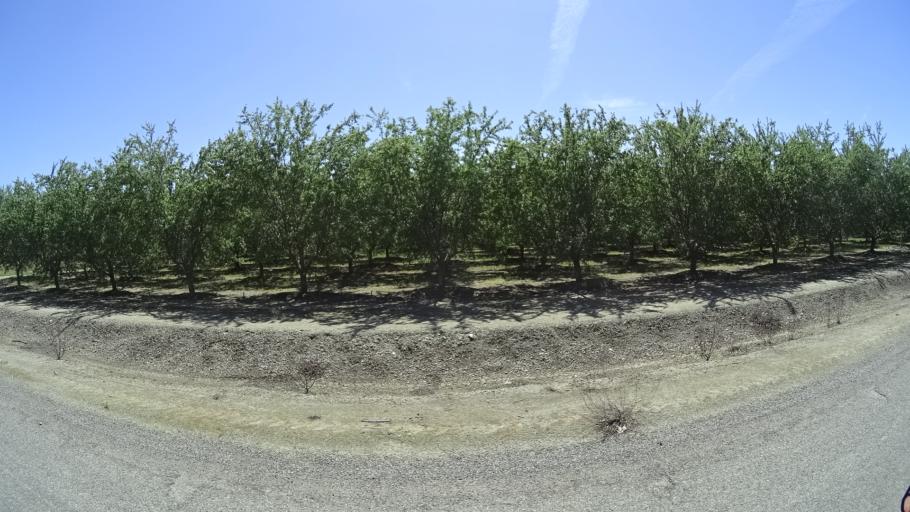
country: US
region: California
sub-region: Glenn County
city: Hamilton City
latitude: 39.7214
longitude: -122.0940
